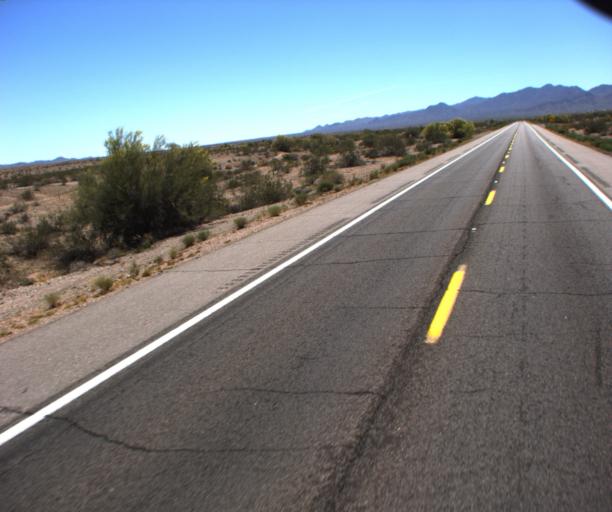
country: US
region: Arizona
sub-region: Mohave County
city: Desert Hills
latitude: 34.7184
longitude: -114.3109
